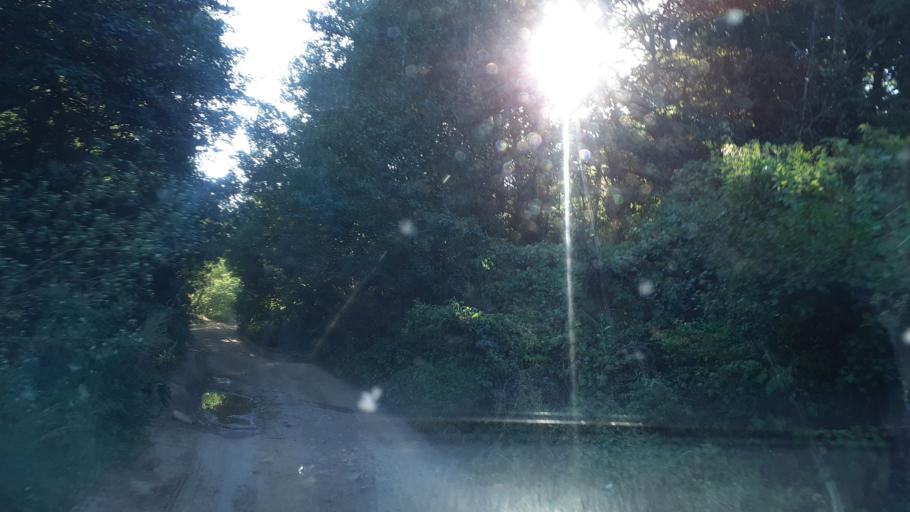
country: RU
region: Krasnodarskiy
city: Azovskaya
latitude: 44.6661
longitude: 38.4992
